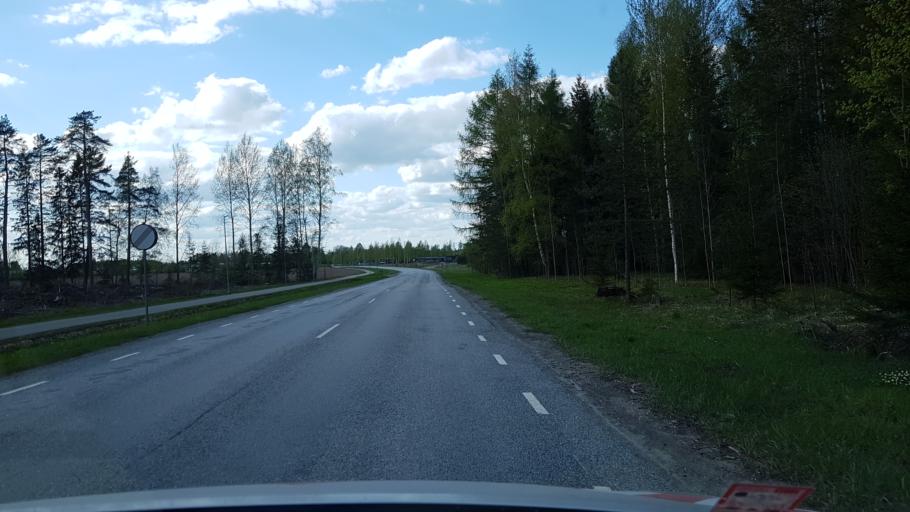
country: EE
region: Tartu
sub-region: UElenurme vald
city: Ulenurme
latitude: 58.3192
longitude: 26.8326
